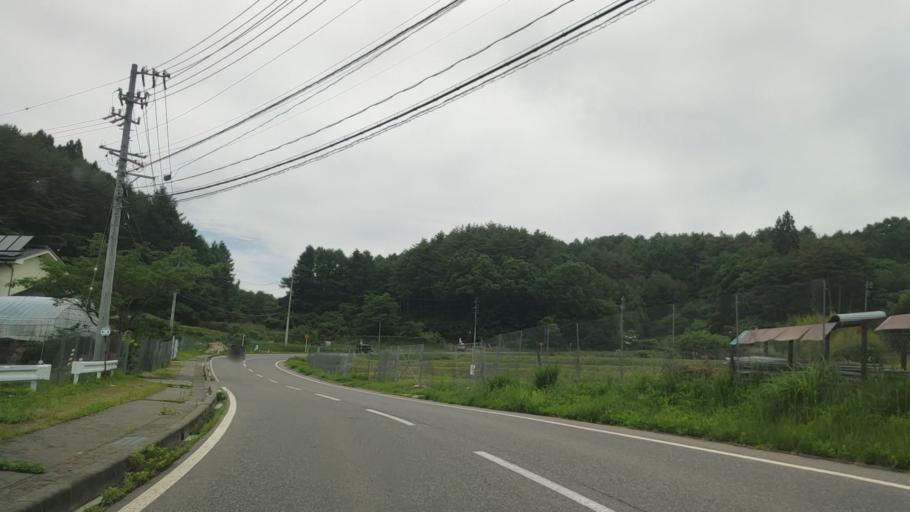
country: JP
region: Nagano
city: Kamimaruko
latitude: 36.2766
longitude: 138.2818
